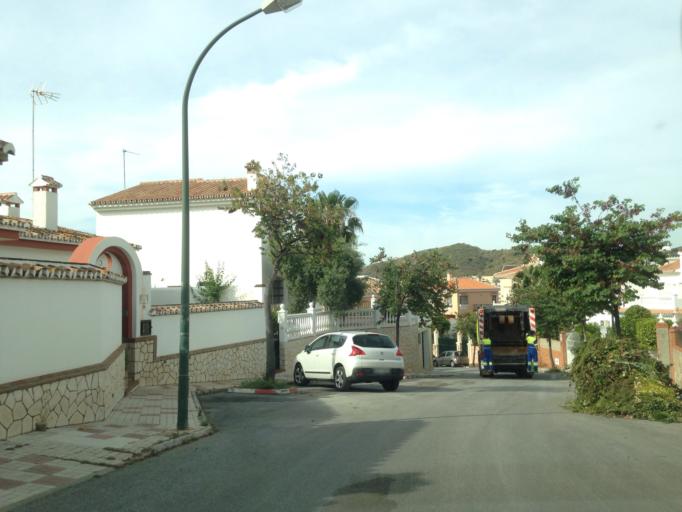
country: ES
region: Andalusia
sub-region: Provincia de Malaga
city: Malaga
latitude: 36.7555
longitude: -4.4237
